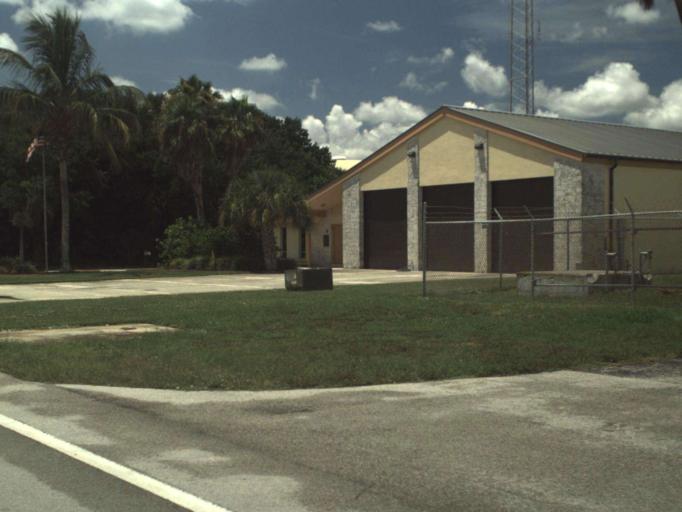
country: US
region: Florida
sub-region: Saint Lucie County
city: Hutchinson Island South
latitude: 27.3282
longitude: -80.2314
